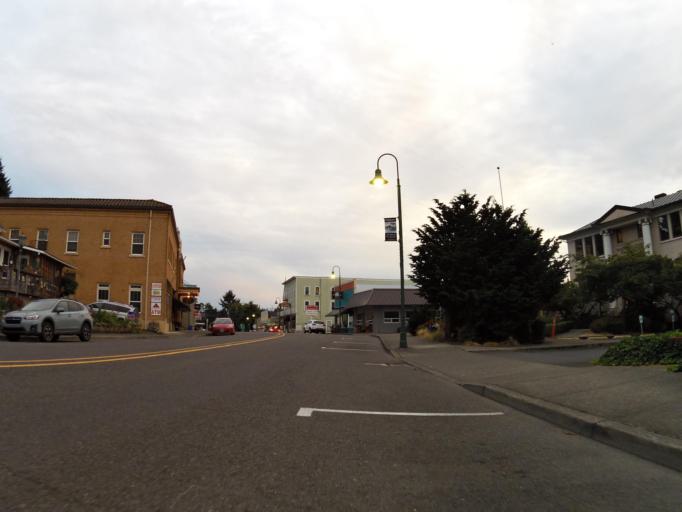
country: US
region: Washington
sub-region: Wahkiakum County
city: Cathlamet
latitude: 46.2029
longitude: -123.3849
